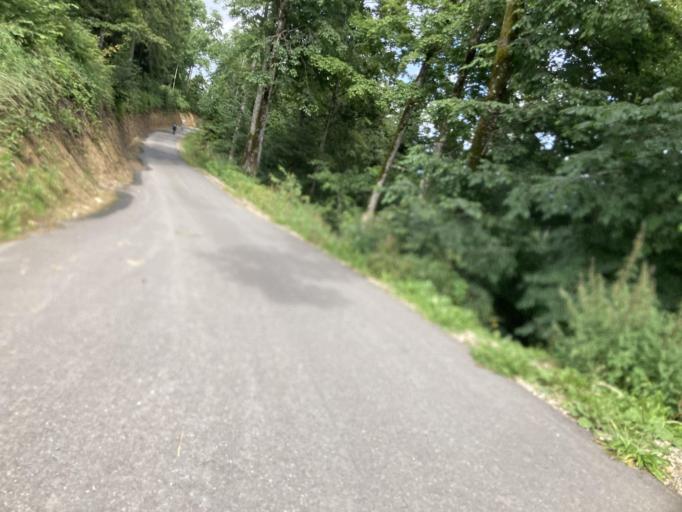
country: CH
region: Thurgau
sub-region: Muenchwilen District
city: Fischingen
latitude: 47.3687
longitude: 8.9427
